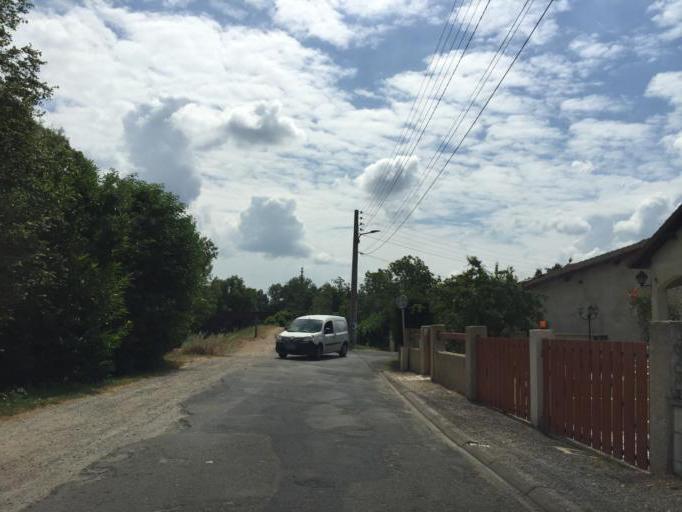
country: FR
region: Auvergne
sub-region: Departement de l'Allier
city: Moulins
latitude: 46.5562
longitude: 3.3249
